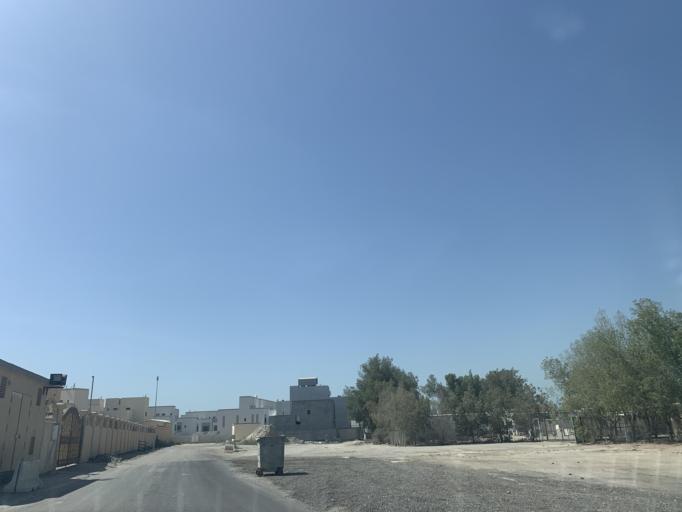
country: BH
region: Manama
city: Jidd Hafs
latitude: 26.2316
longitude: 50.4986
